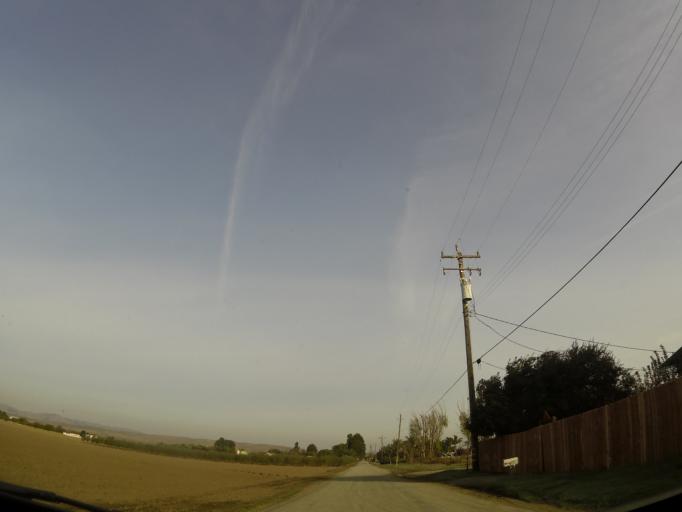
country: US
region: California
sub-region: San Benito County
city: San Juan Bautista
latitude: 36.8460
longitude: -121.4724
